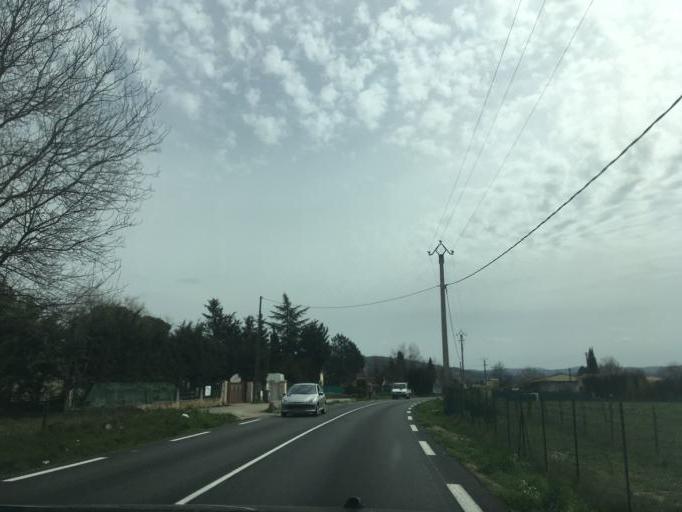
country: FR
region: Provence-Alpes-Cote d'Azur
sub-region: Departement du Var
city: Callian
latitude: 43.6077
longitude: 6.7456
